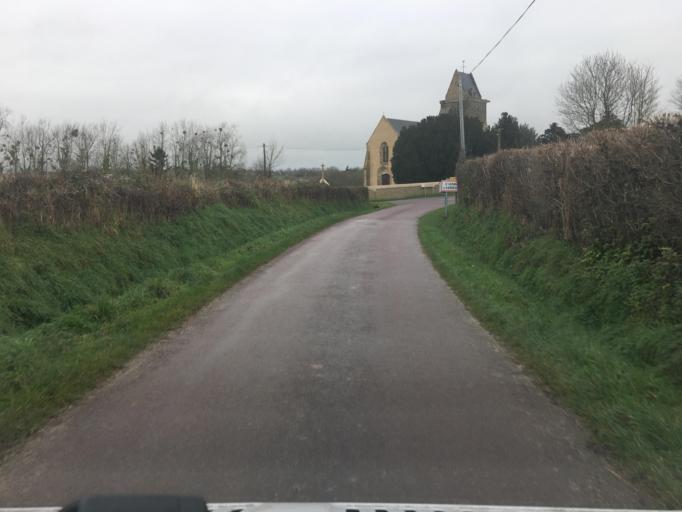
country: FR
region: Lower Normandy
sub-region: Departement de la Manche
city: Sainte-Mere-Eglise
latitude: 49.4364
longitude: -1.2595
